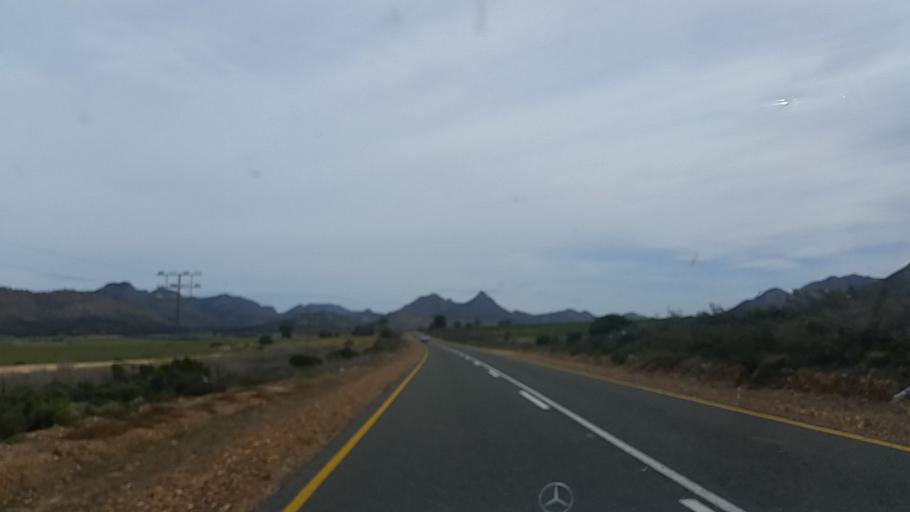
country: ZA
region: Western Cape
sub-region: Eden District Municipality
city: George
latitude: -33.8204
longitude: 22.4948
